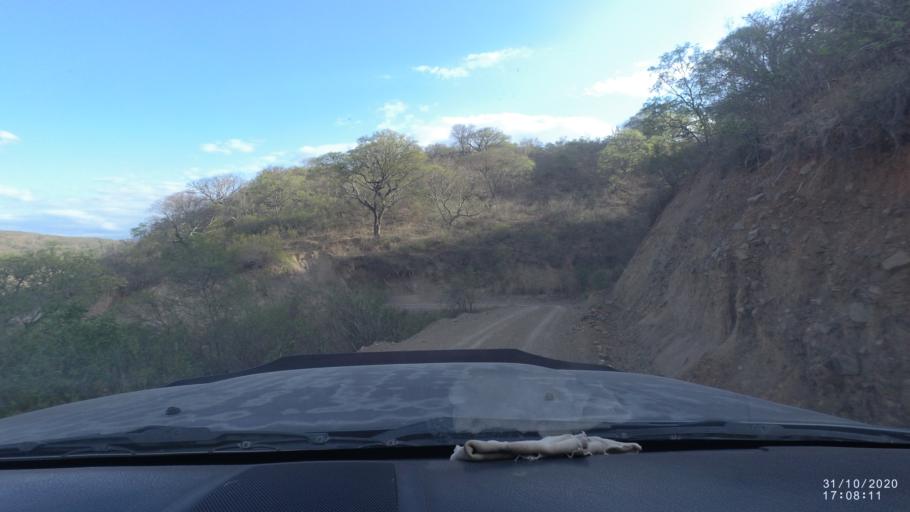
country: BO
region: Chuquisaca
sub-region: Provincia Zudanez
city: Mojocoya
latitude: -18.5460
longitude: -64.5406
